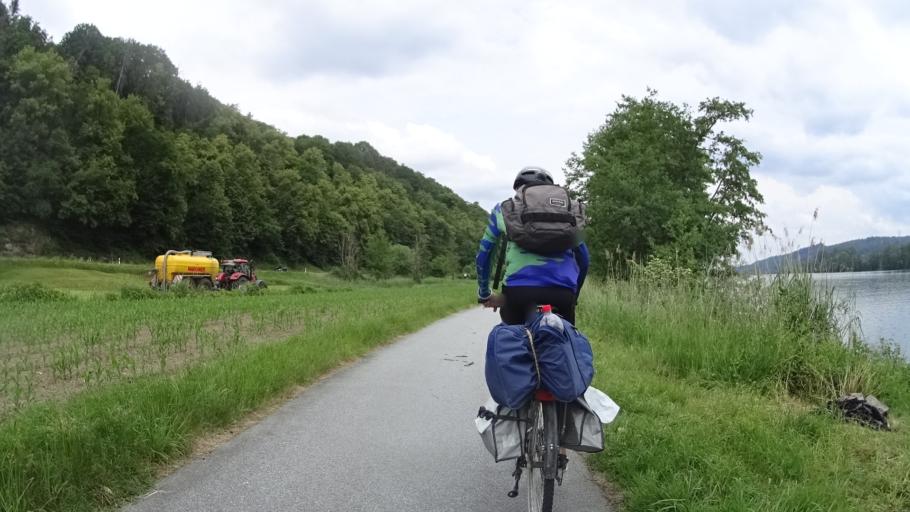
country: DE
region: Bavaria
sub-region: Lower Bavaria
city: Aicha vorm Wald
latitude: 48.6128
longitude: 13.2807
